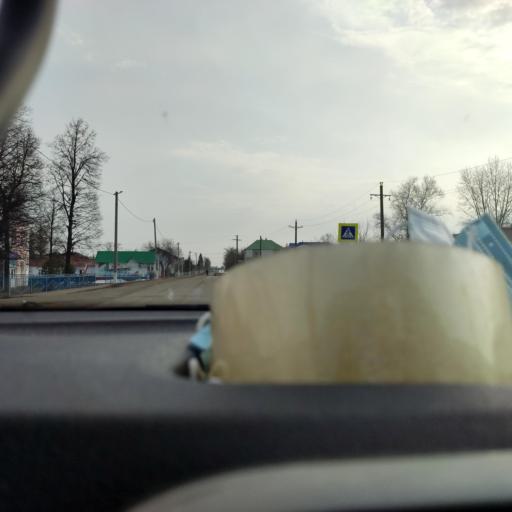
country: RU
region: Bashkortostan
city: Ulukulevo
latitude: 54.3773
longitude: 56.4496
